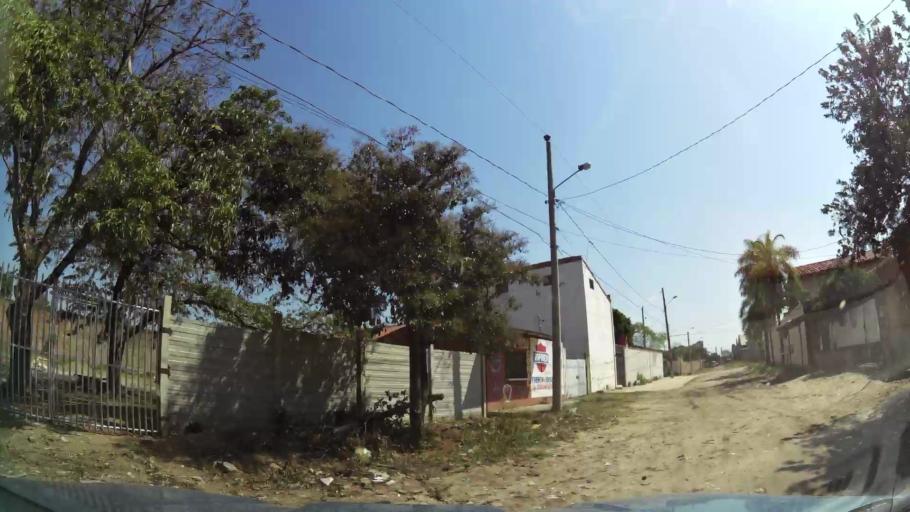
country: BO
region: Santa Cruz
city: Santa Cruz de la Sierra
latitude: -17.7305
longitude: -63.1555
